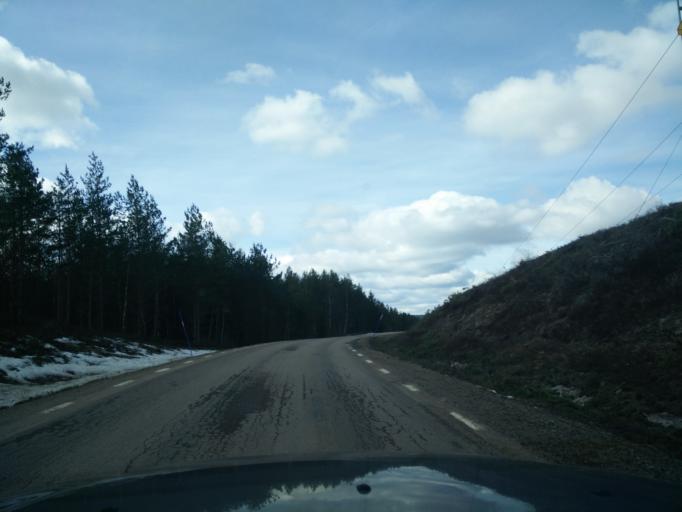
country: SE
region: Vaermland
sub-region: Hagfors Kommun
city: Hagfors
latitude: 60.0345
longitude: 13.5619
